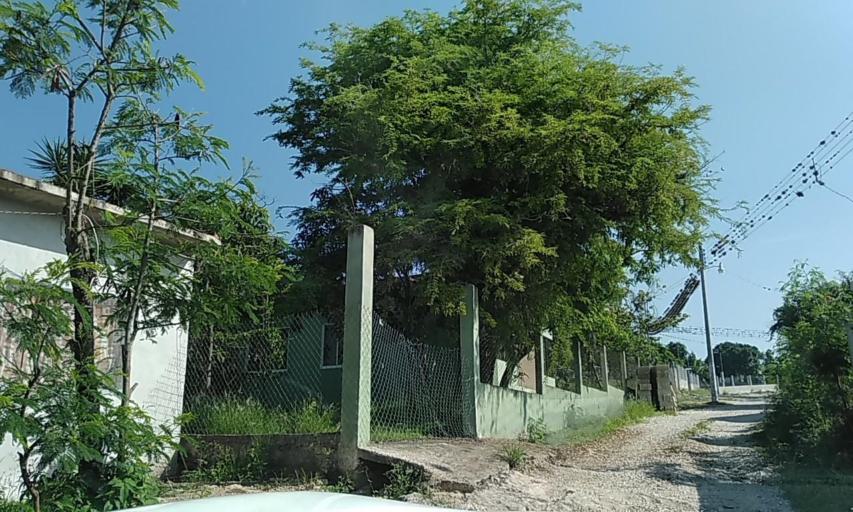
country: MX
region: Veracruz
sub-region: Emiliano Zapata
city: Plan del Rio
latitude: 19.4532
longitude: -96.6796
